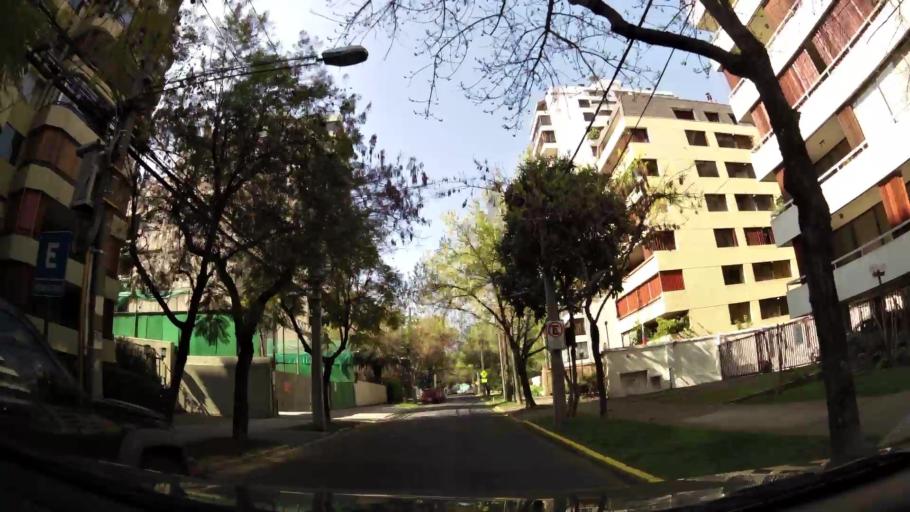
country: CL
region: Santiago Metropolitan
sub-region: Provincia de Santiago
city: Villa Presidente Frei, Nunoa, Santiago, Chile
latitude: -33.4050
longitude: -70.5948
